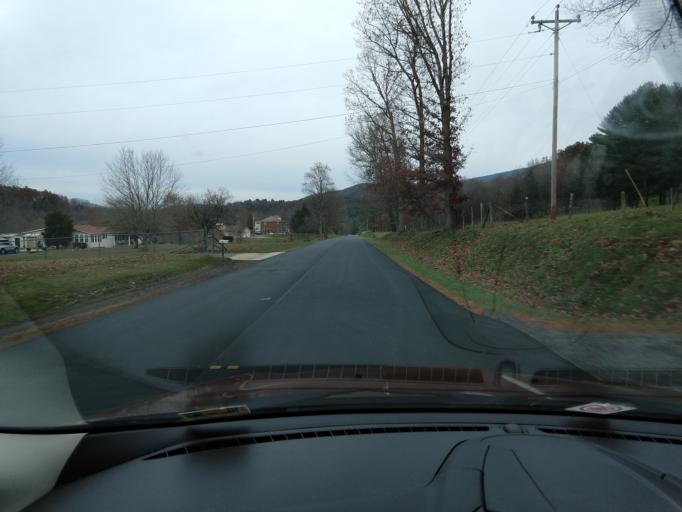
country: US
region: West Virginia
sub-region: Greenbrier County
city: White Sulphur Springs
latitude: 37.7388
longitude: -80.1833
